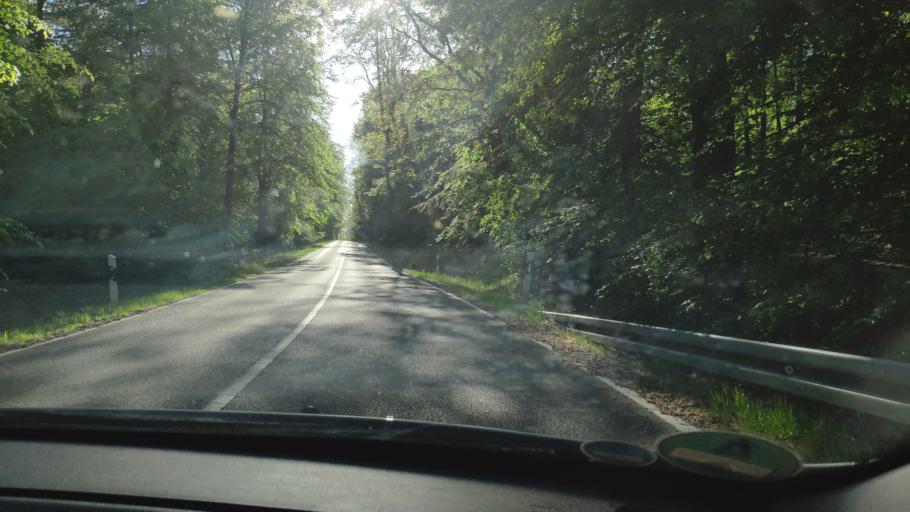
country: DE
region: Mecklenburg-Vorpommern
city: Wesenberg
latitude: 53.3211
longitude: 12.9582
